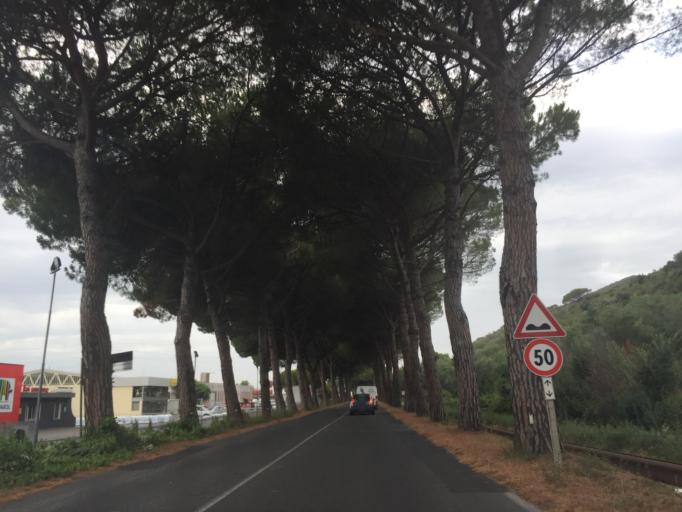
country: IT
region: Tuscany
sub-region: Province of Pisa
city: Uliveto Terme
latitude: 43.6880
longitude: 10.5394
